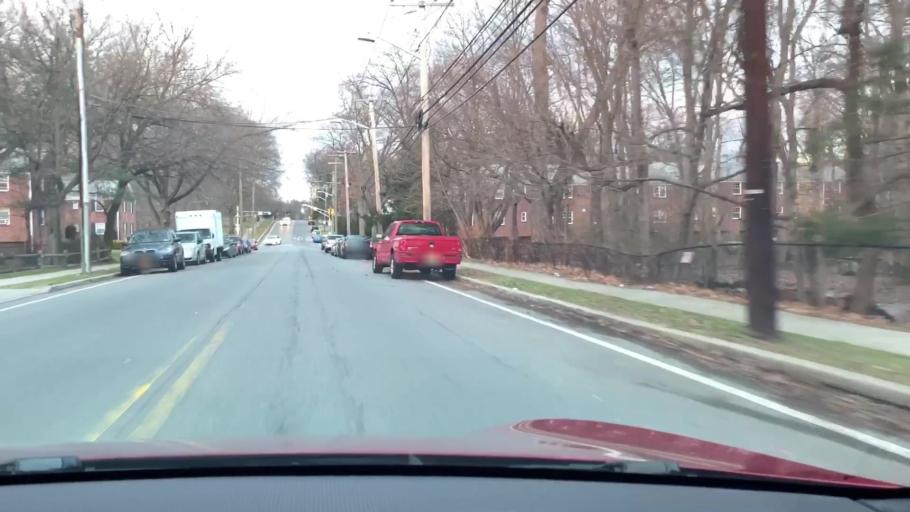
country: US
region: New Jersey
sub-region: Bergen County
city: Englewood
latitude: 40.9040
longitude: -73.9804
